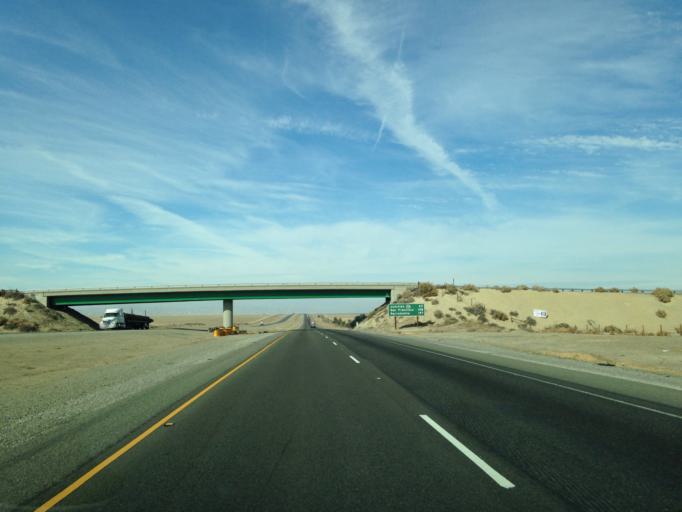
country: US
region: California
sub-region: Fresno County
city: Mendota
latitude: 36.5529
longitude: -120.5170
